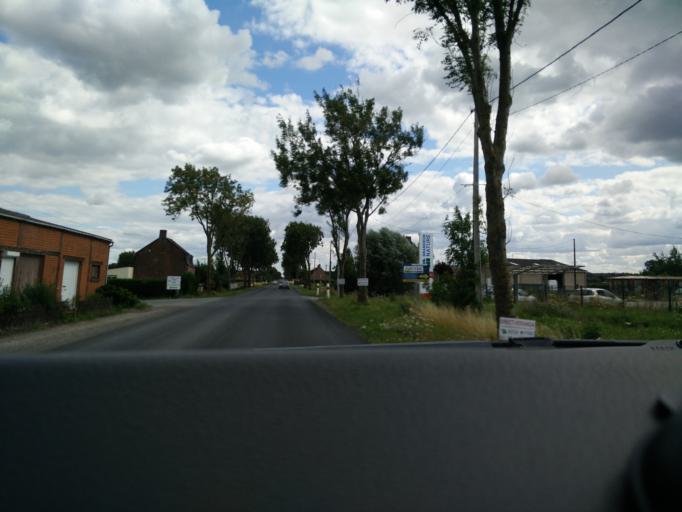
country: FR
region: Nord-Pas-de-Calais
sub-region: Departement du Nord
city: Morbecque
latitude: 50.6798
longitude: 2.5137
